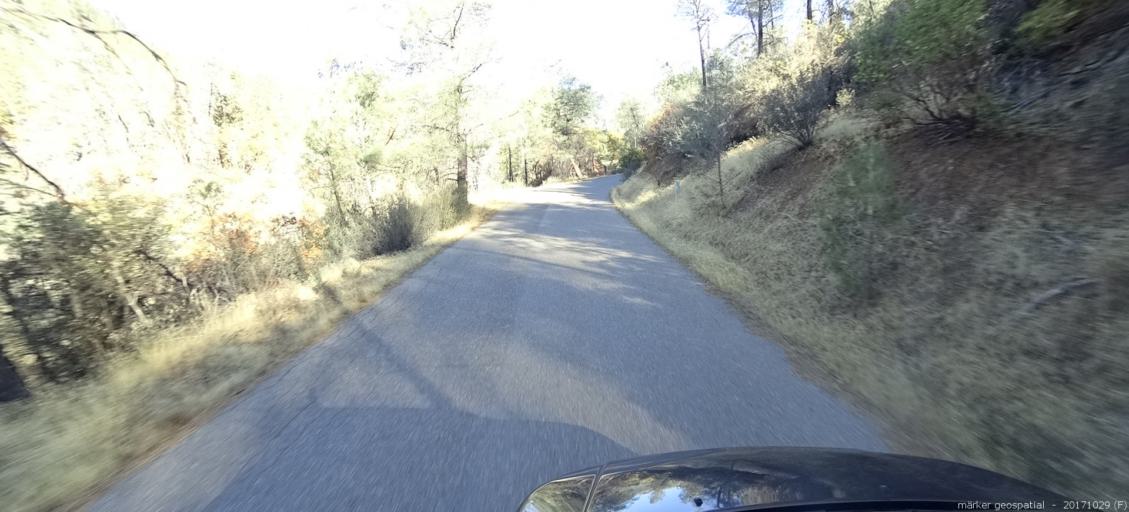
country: US
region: California
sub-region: Trinity County
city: Hayfork
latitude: 40.3731
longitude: -122.9759
